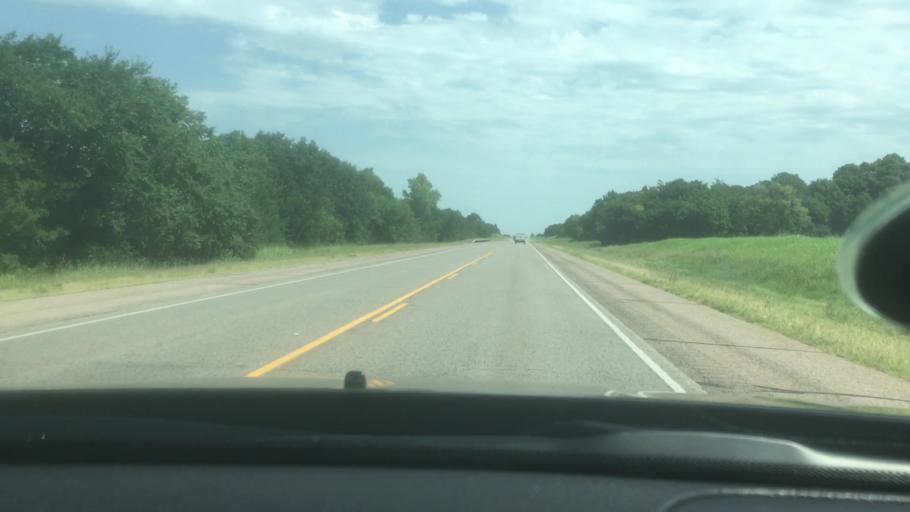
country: US
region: Oklahoma
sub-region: Seminole County
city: Konawa
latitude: 35.0104
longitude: -96.9316
